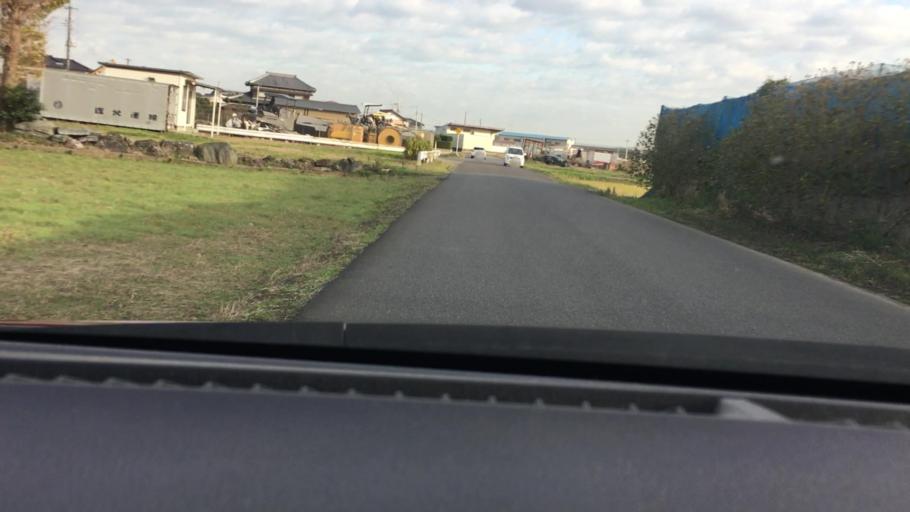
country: JP
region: Chiba
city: Kisarazu
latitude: 35.4039
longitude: 139.9596
